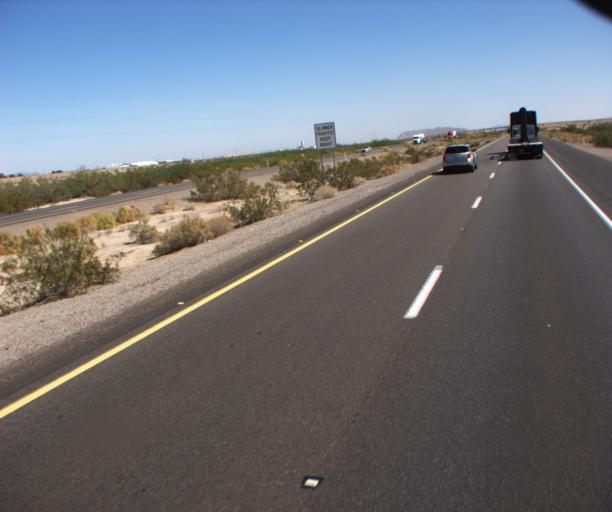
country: US
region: Arizona
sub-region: Yuma County
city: Wellton
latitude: 32.6672
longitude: -114.1190
